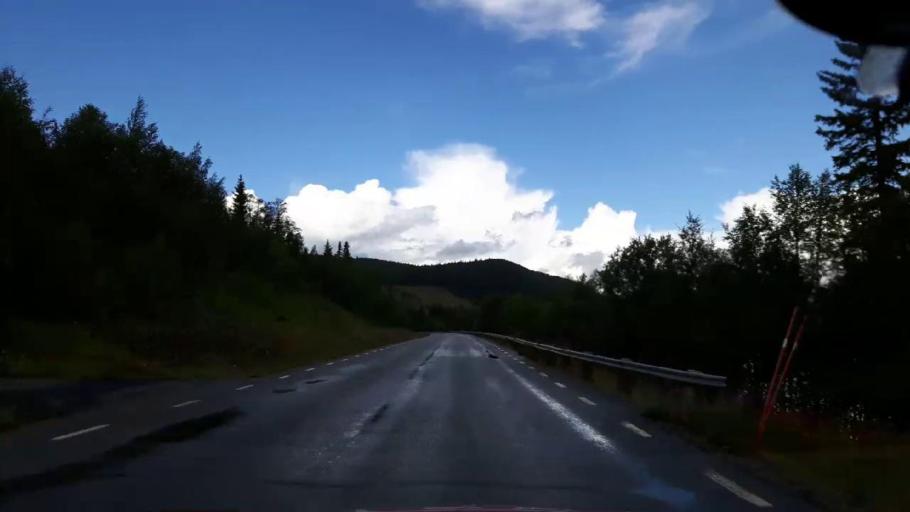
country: SE
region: Vaesterbotten
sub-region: Vilhelmina Kommun
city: Sjoberg
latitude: 64.9944
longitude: 15.2216
